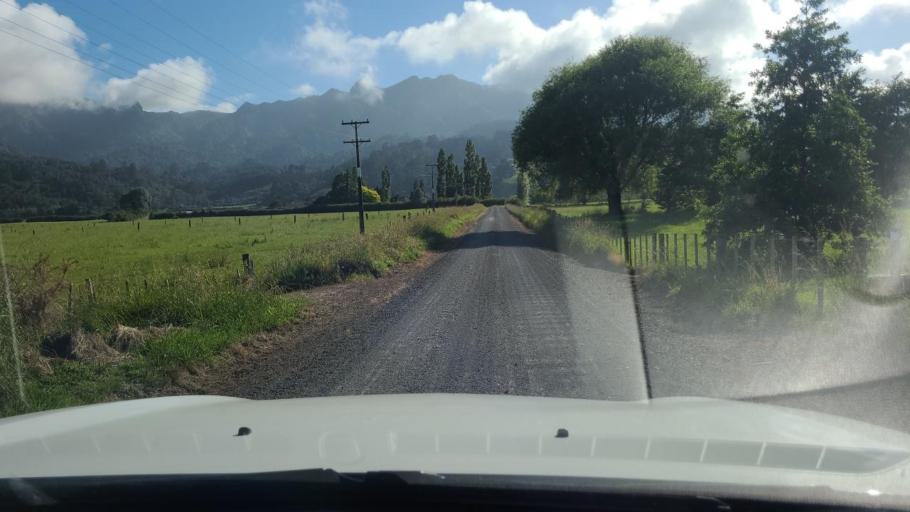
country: NZ
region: Bay of Plenty
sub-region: Western Bay of Plenty District
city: Katikati
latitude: -37.5763
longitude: 175.7591
